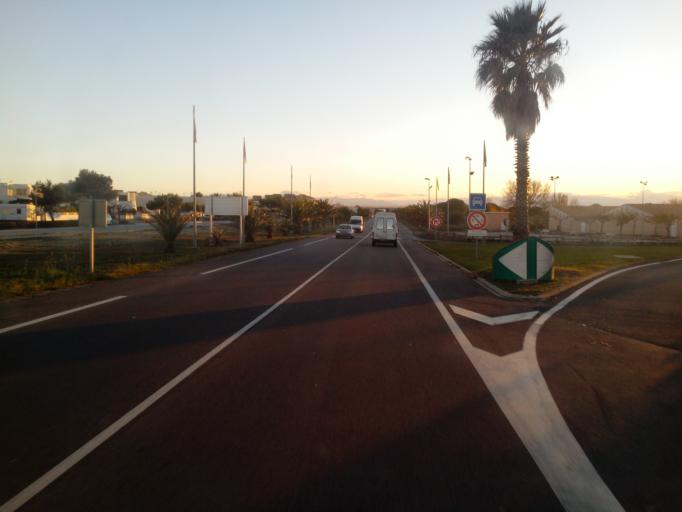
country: FR
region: Languedoc-Roussillon
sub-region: Departement des Pyrenees-Orientales
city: Le Barcares
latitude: 42.8376
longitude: 3.0388
